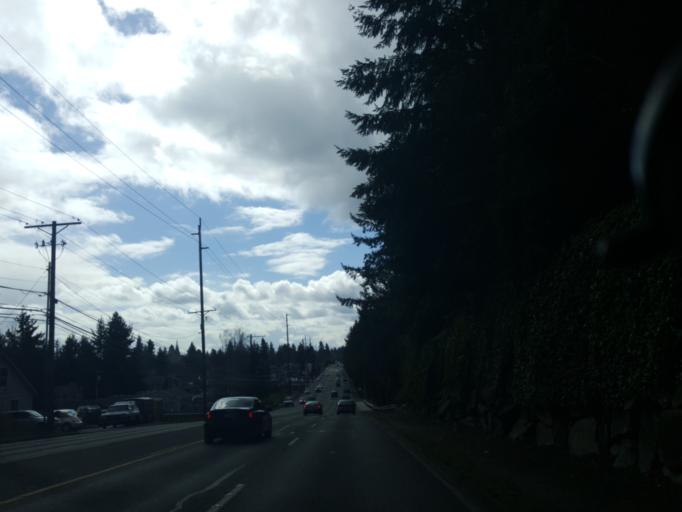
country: US
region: Washington
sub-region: Pierce County
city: Lakewood
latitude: 47.2013
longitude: -122.5087
